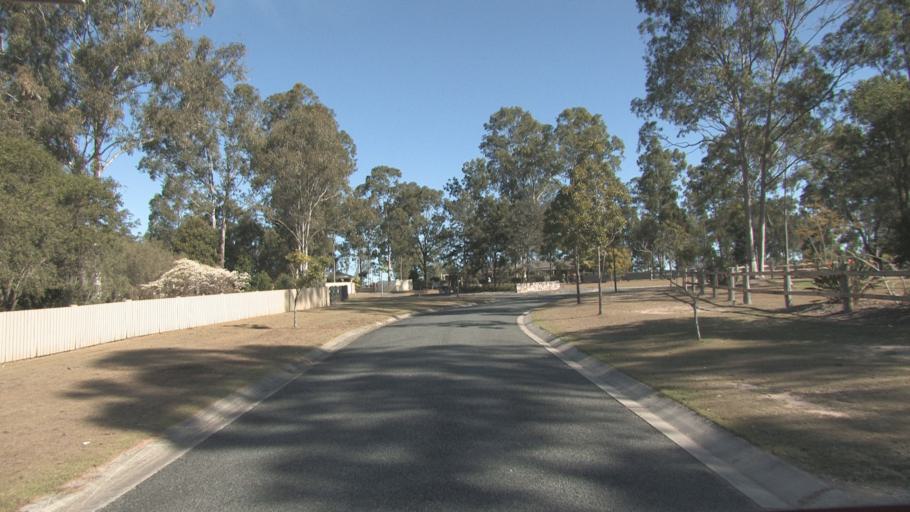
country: AU
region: Queensland
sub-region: Logan
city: North Maclean
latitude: -27.8093
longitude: 152.9609
